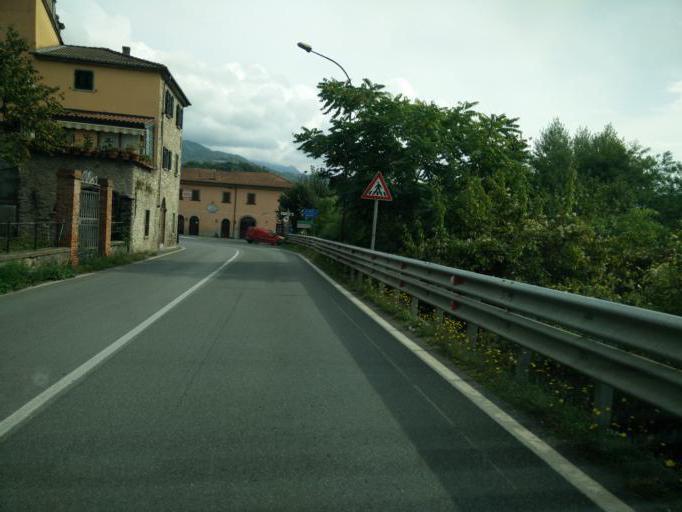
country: IT
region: Tuscany
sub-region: Provincia di Massa-Carrara
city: Pontremoli
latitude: 44.3636
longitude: 9.8875
